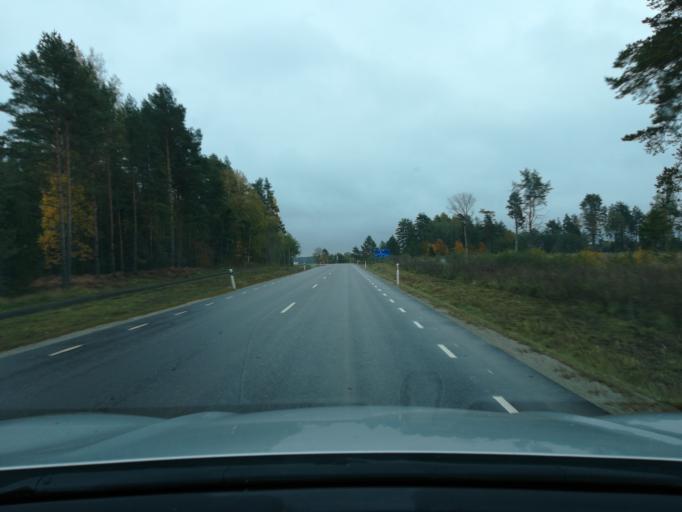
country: EE
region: Ida-Virumaa
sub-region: Johvi vald
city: Johvi
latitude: 59.2959
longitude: 27.4878
